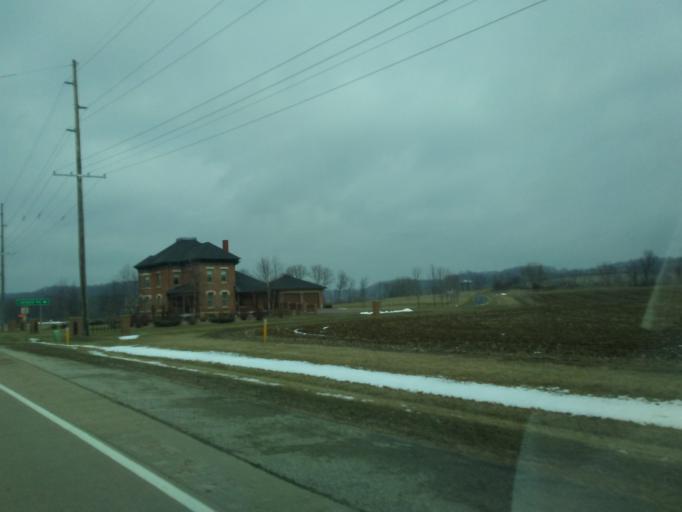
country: US
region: Wisconsin
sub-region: Richland County
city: Richland Center
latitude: 43.3097
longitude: -90.3386
